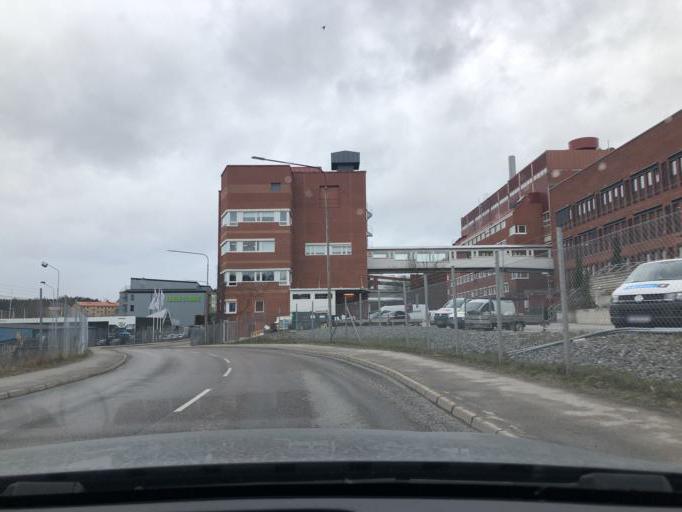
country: SE
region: Stockholm
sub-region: Sodertalje Kommun
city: Soedertaelje
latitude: 59.2033
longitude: 17.6142
